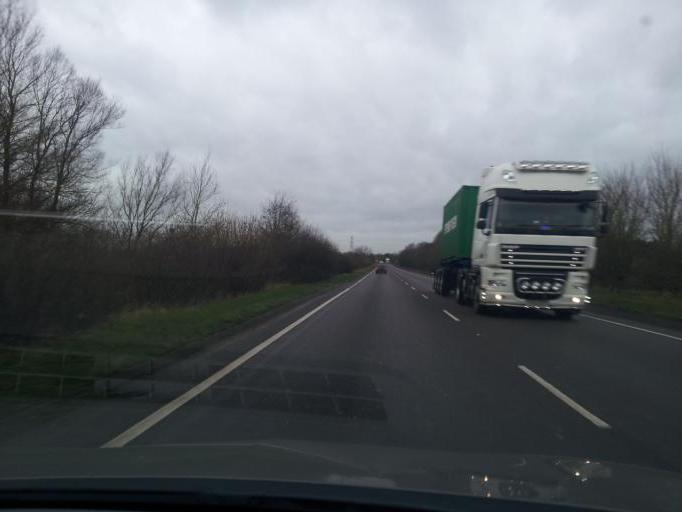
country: GB
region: England
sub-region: Norfolk
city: Diss
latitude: 52.3628
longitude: 1.1621
